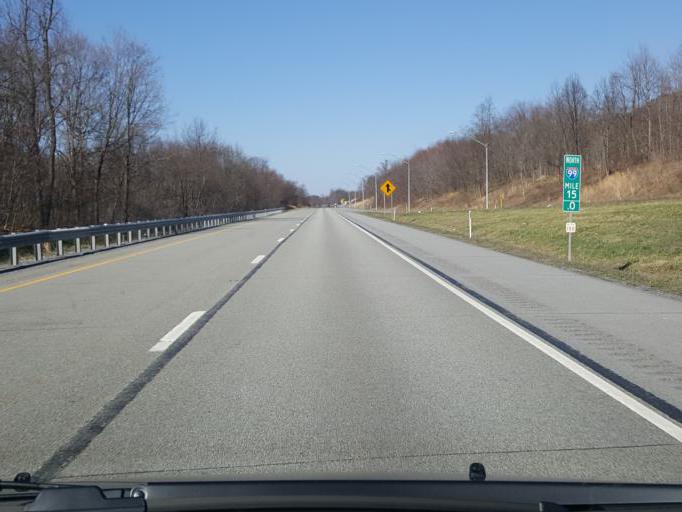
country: US
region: Pennsylvania
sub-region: Blair County
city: Claysburg
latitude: 40.2597
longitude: -78.4561
